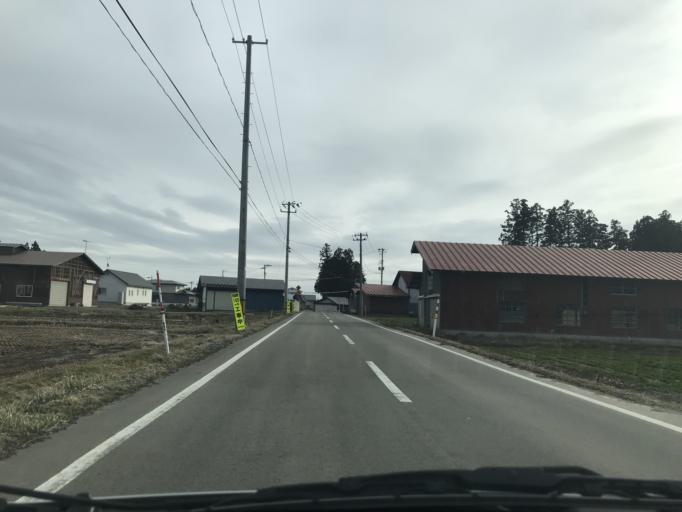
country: JP
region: Iwate
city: Hanamaki
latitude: 39.3466
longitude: 141.0595
